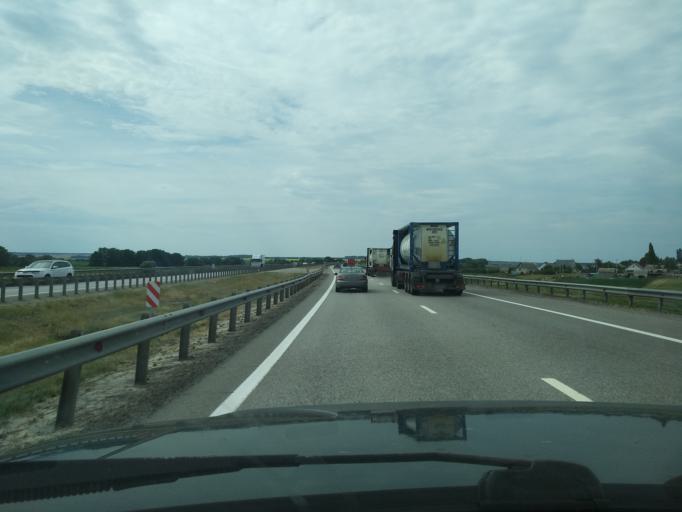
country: RU
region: Lipetsk
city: Khlevnoye
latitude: 52.0572
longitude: 39.1901
